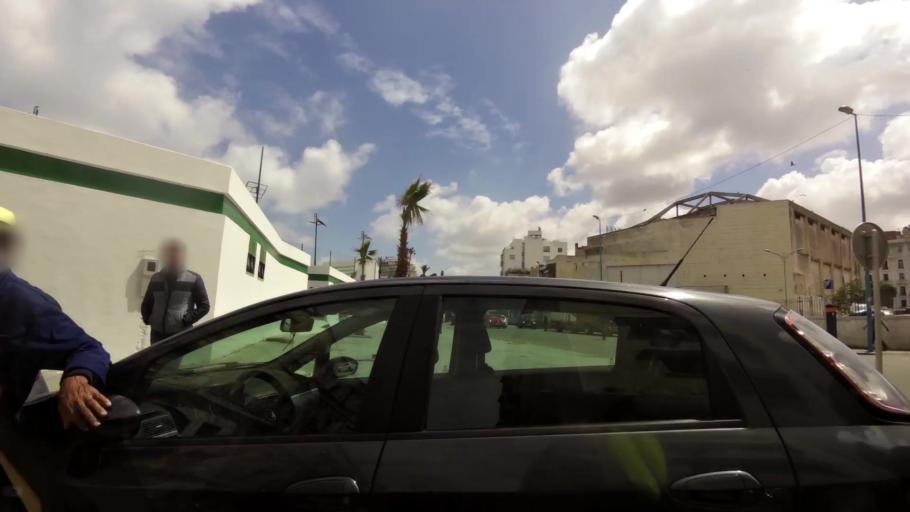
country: MA
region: Grand Casablanca
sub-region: Casablanca
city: Casablanca
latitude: 33.5952
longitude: -7.6226
